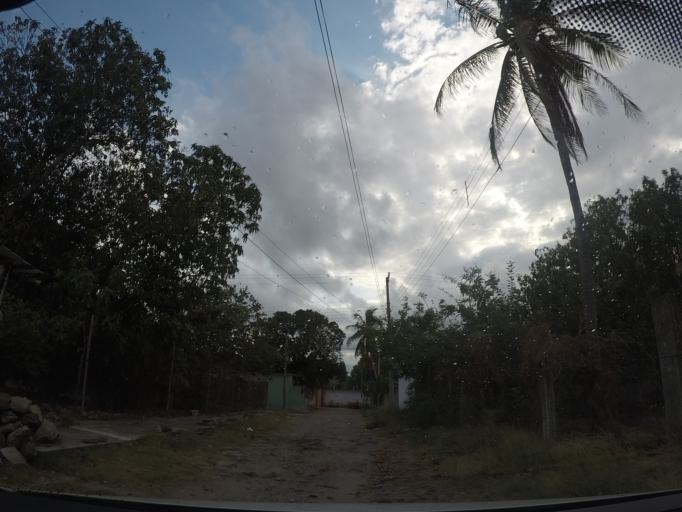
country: MX
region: Oaxaca
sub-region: Salina Cruz
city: Salina Cruz
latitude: 16.2092
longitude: -95.2065
